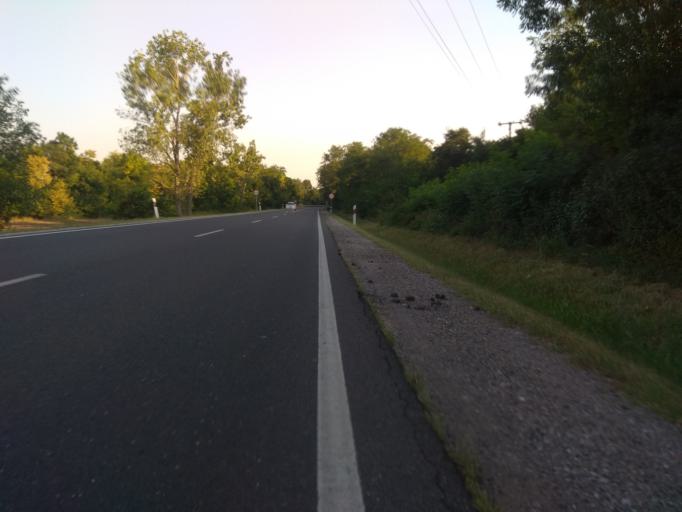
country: HU
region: Borsod-Abauj-Zemplen
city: Nyekladhaza
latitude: 47.9613
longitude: 20.8343
